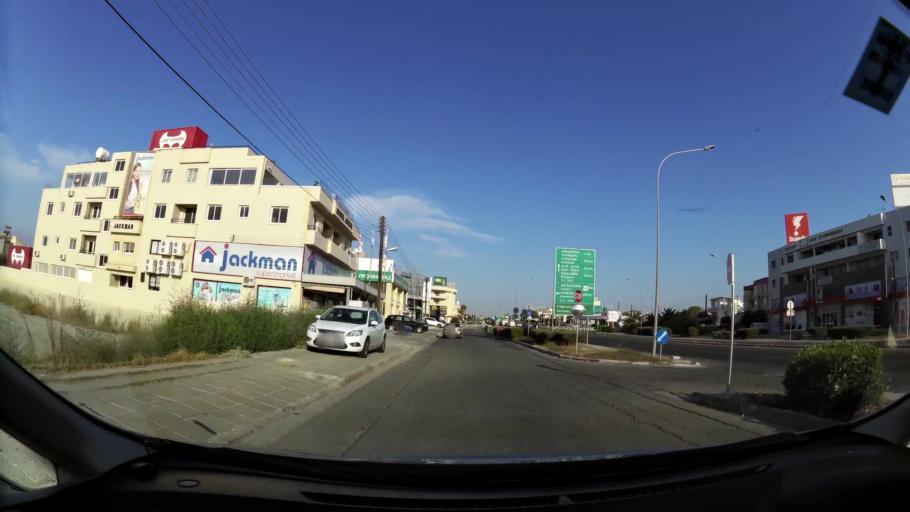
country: CY
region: Larnaka
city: Aradippou
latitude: 34.9319
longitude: 33.5969
